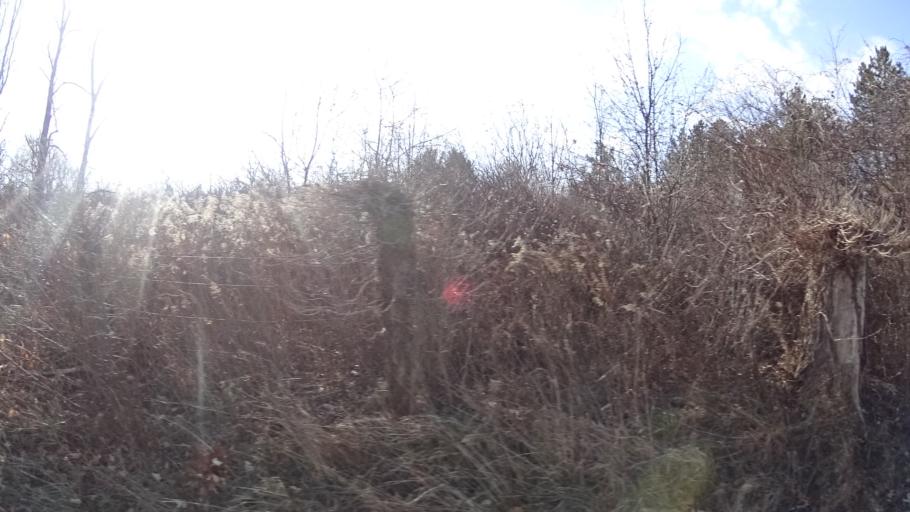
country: US
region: Ohio
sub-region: Lorain County
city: Wellington
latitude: 41.2101
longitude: -82.2539
